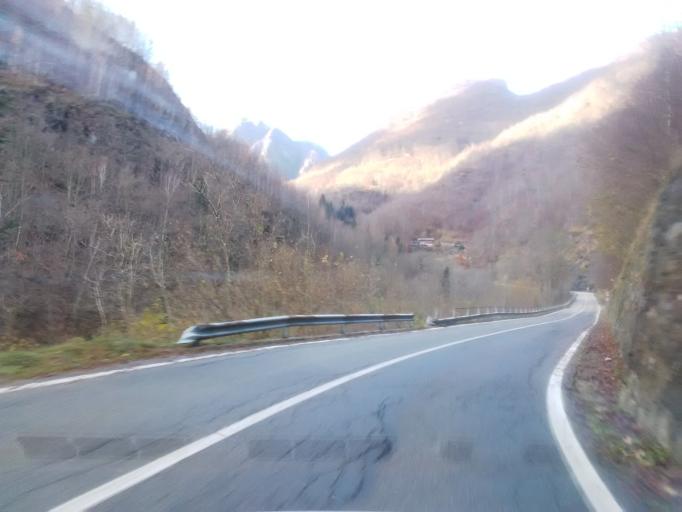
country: IT
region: Piedmont
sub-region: Provincia di Vercelli
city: Cravagliana
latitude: 45.8455
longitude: 8.1970
